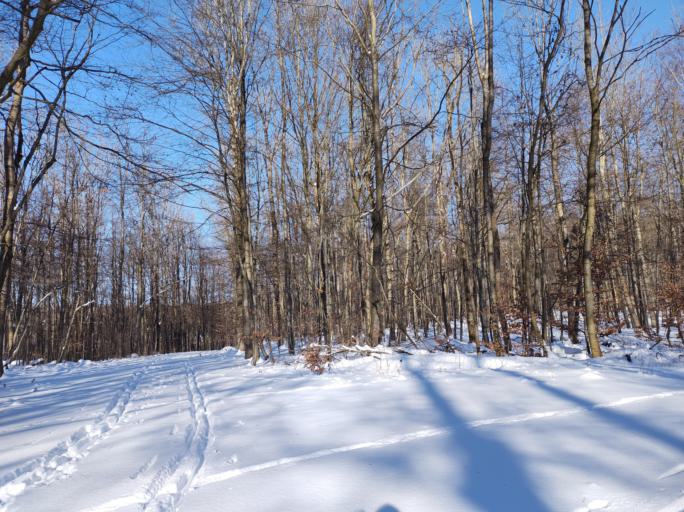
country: DE
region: North Rhine-Westphalia
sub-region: Regierungsbezirk Detmold
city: Schlangen
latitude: 51.8226
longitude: 8.8922
